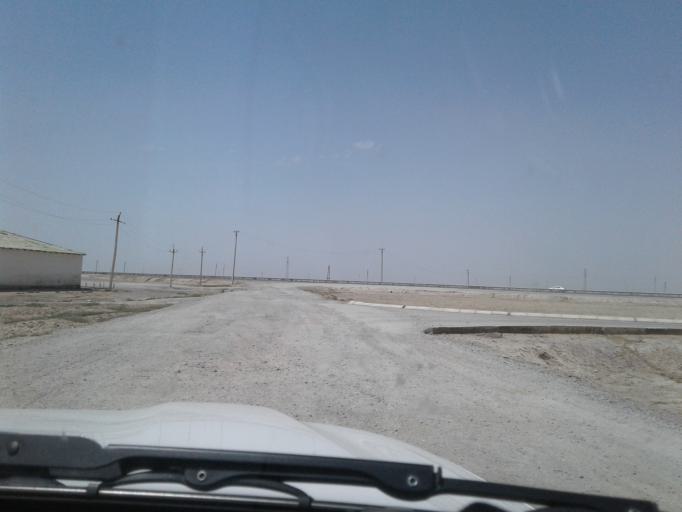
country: IR
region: Razavi Khorasan
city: Kalat-e Naderi
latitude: 37.2056
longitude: 60.0231
